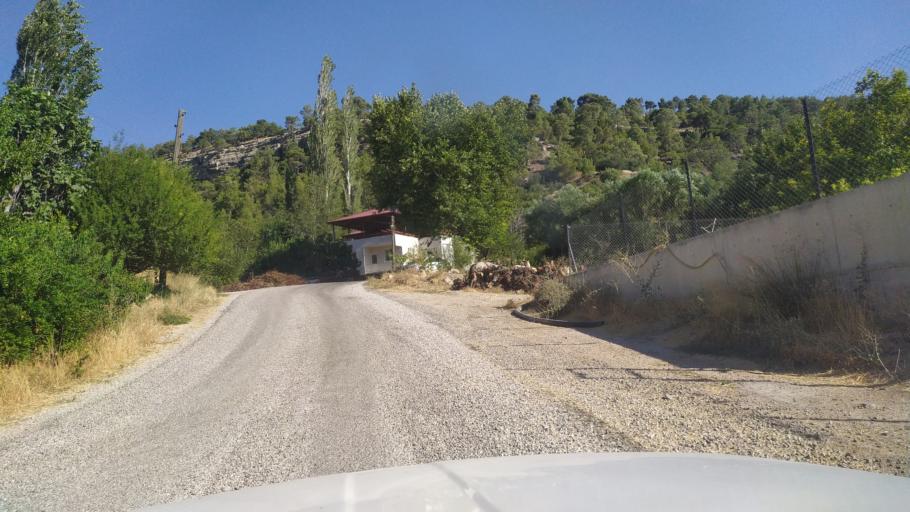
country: TR
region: Mersin
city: Mut
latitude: 36.7058
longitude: 33.4737
